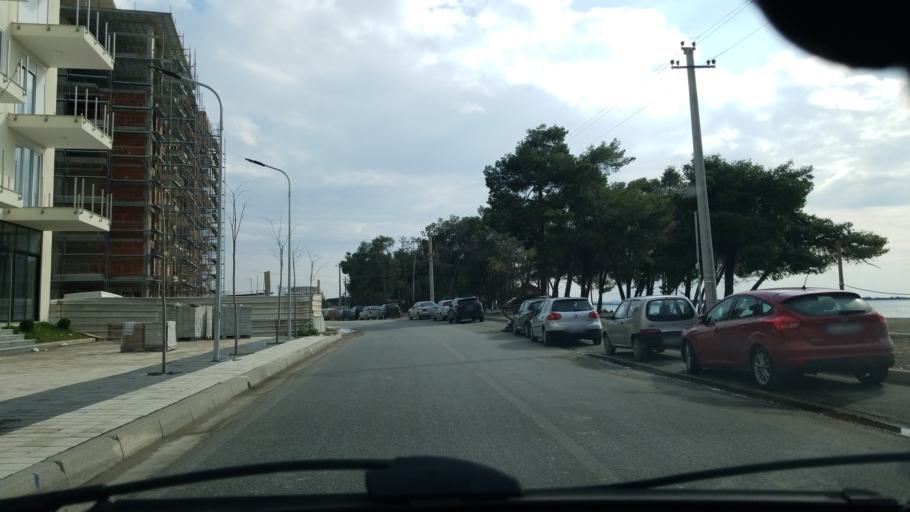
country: AL
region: Lezhe
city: Shengjin
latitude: 41.7932
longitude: 19.6026
